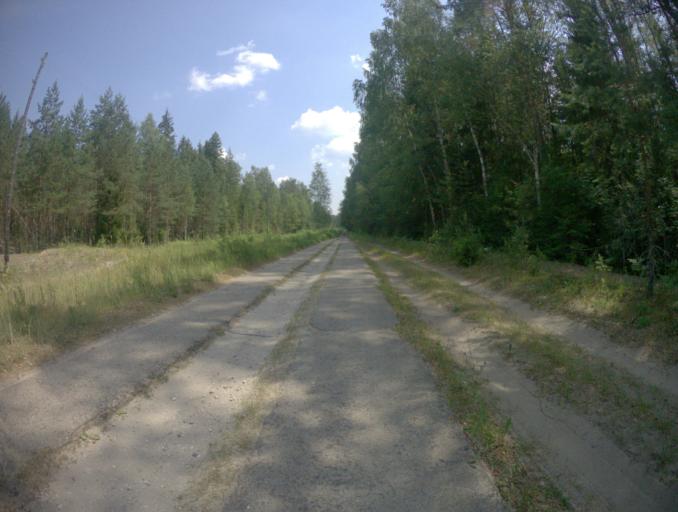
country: RU
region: Nizjnij Novgorod
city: Frolishchi
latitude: 56.4002
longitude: 42.5584
